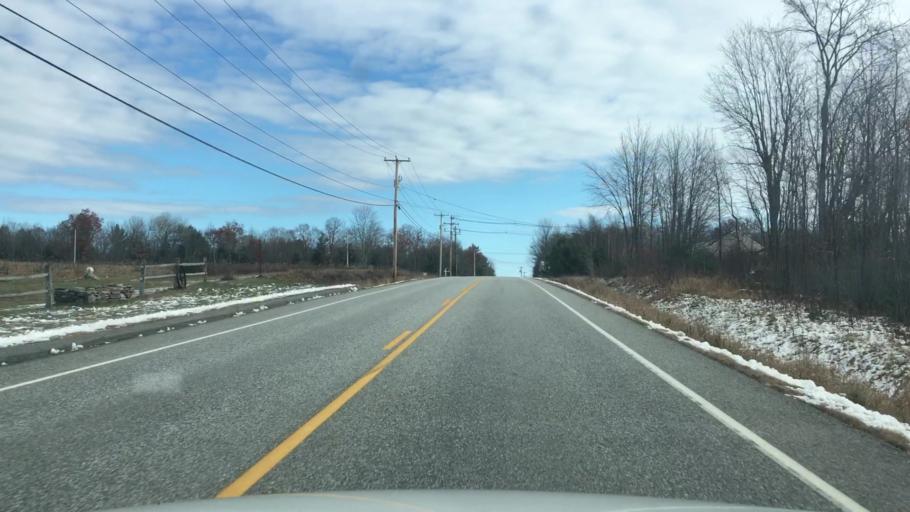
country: US
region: Maine
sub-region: Androscoggin County
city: Leeds
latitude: 44.3436
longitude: -70.1729
